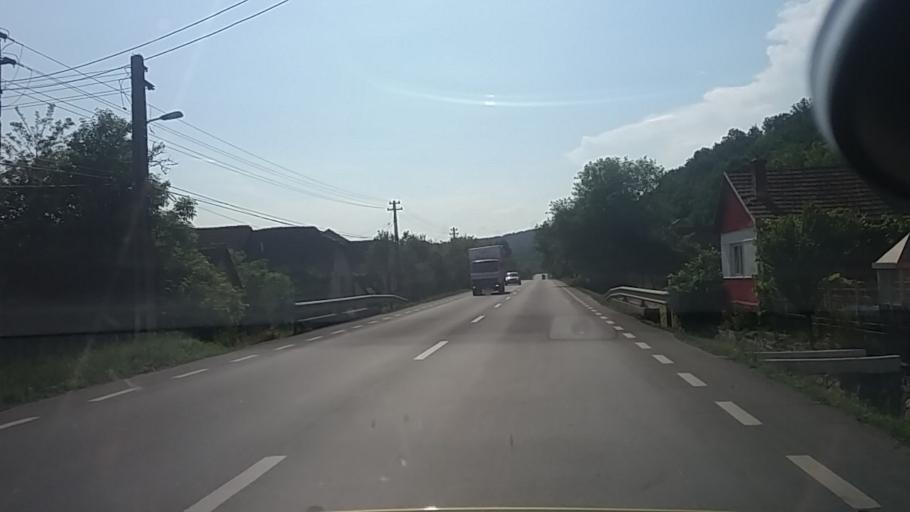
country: RO
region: Arad
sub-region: Comuna Ususau
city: Ususau
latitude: 46.1117
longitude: 21.8326
